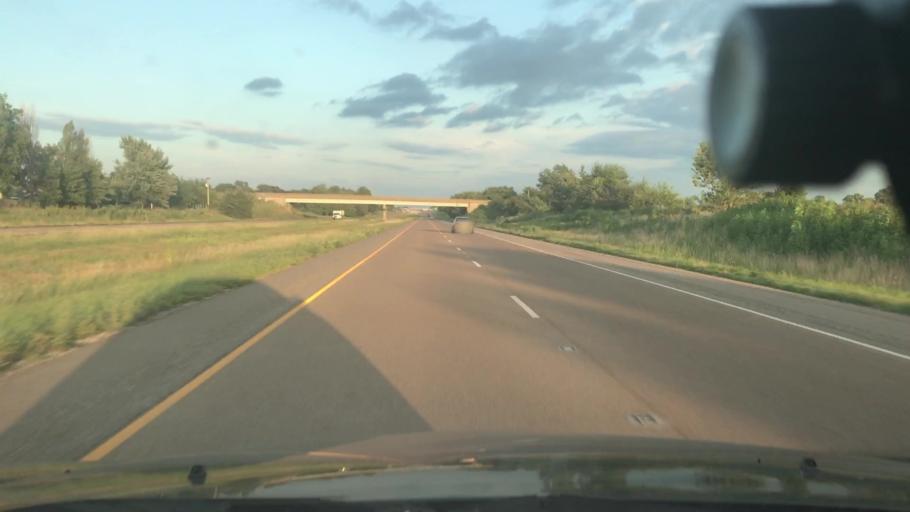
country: US
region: Illinois
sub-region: Washington County
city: Okawville
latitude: 38.4496
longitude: -89.5492
